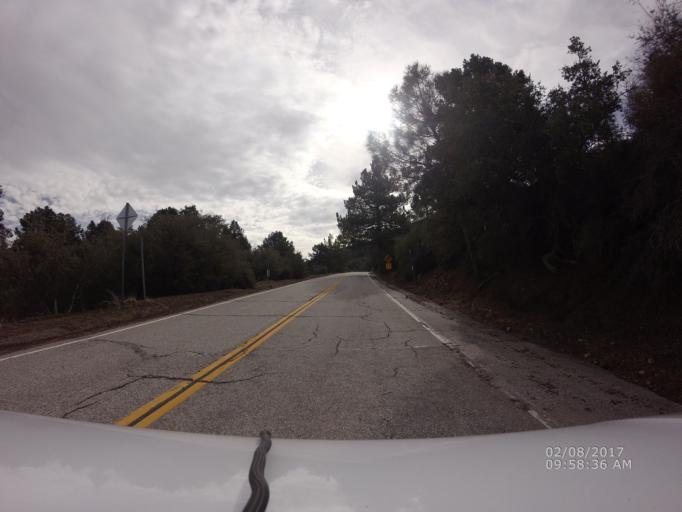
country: US
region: California
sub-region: San Bernardino County
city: Pinon Hills
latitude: 34.4106
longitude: -117.7713
